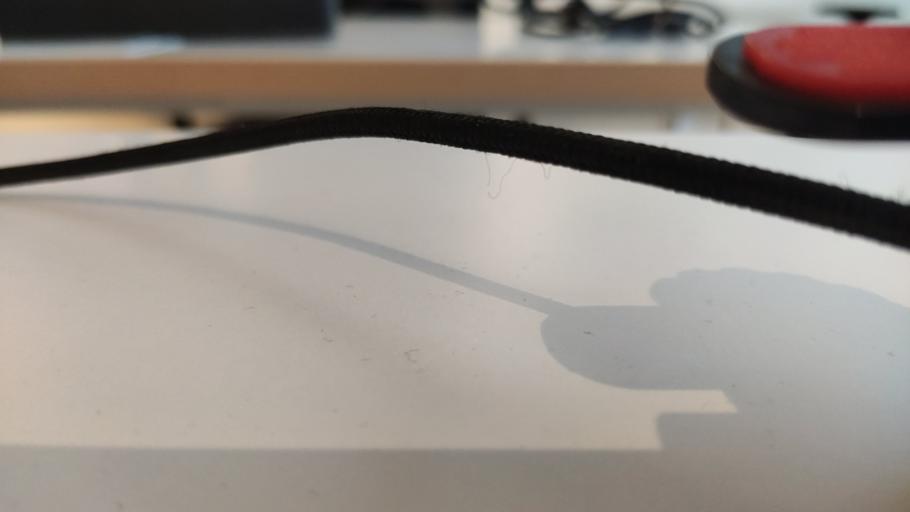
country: RU
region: Moskovskaya
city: Novopetrovskoye
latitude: 55.9692
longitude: 36.4412
